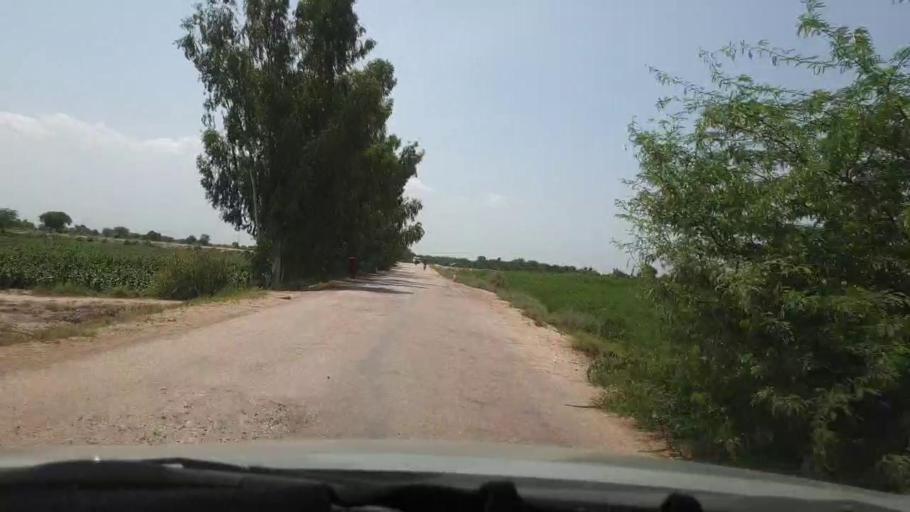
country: PK
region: Sindh
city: Rohri
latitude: 27.6696
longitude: 69.0812
